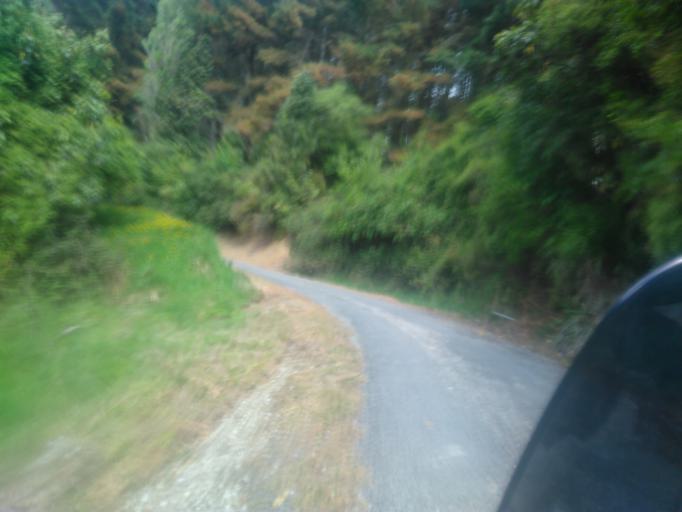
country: NZ
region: Hawke's Bay
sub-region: Wairoa District
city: Wairoa
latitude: -38.7666
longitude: 177.5923
